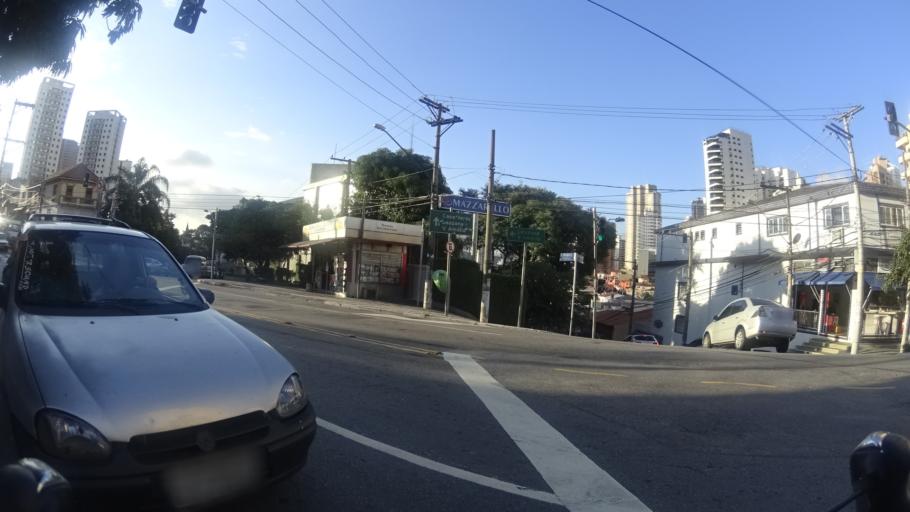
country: BR
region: Sao Paulo
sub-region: Sao Paulo
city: Sao Paulo
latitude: -23.4928
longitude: -46.6328
